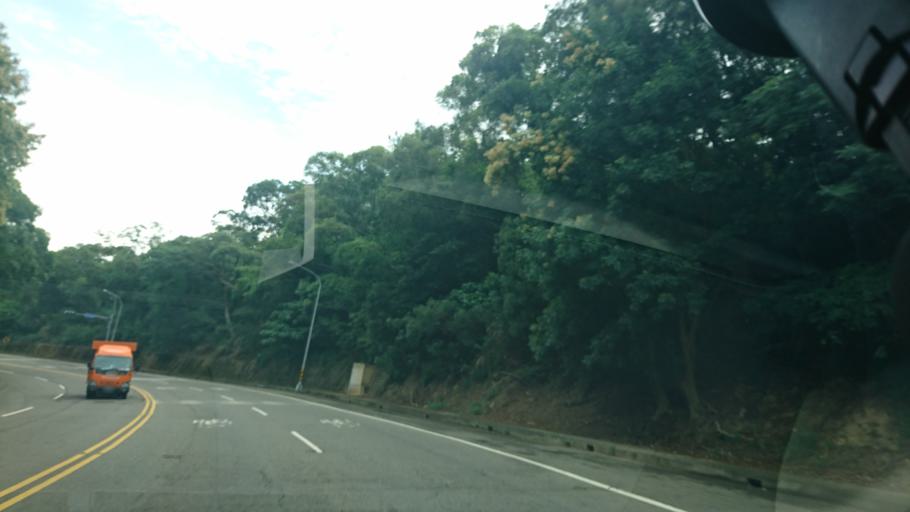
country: TW
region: Taiwan
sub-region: Miaoli
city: Miaoli
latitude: 24.5394
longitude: 120.8106
